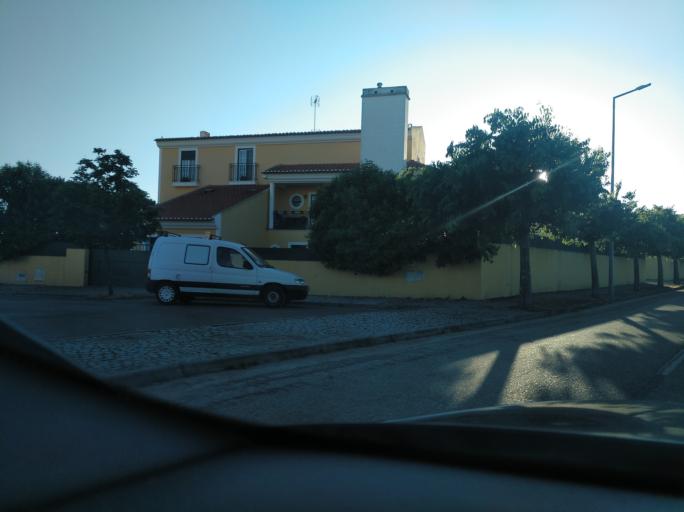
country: PT
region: Portalegre
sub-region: Elvas
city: Elvas
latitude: 38.8763
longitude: -7.1913
